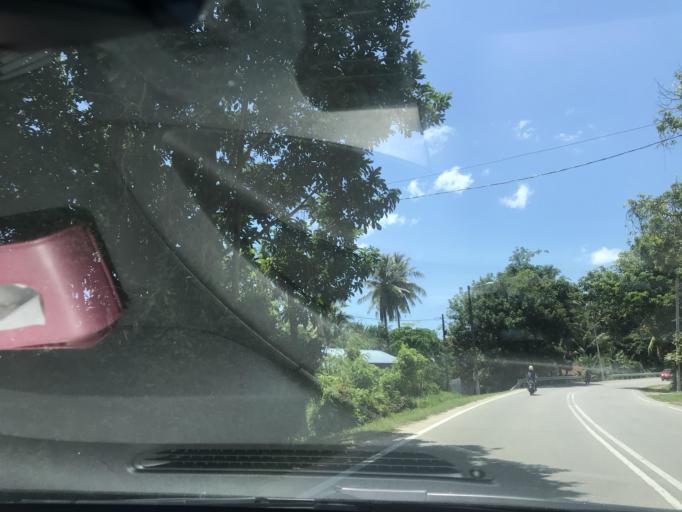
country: MY
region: Kelantan
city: Tumpat
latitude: 6.1933
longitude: 102.1480
